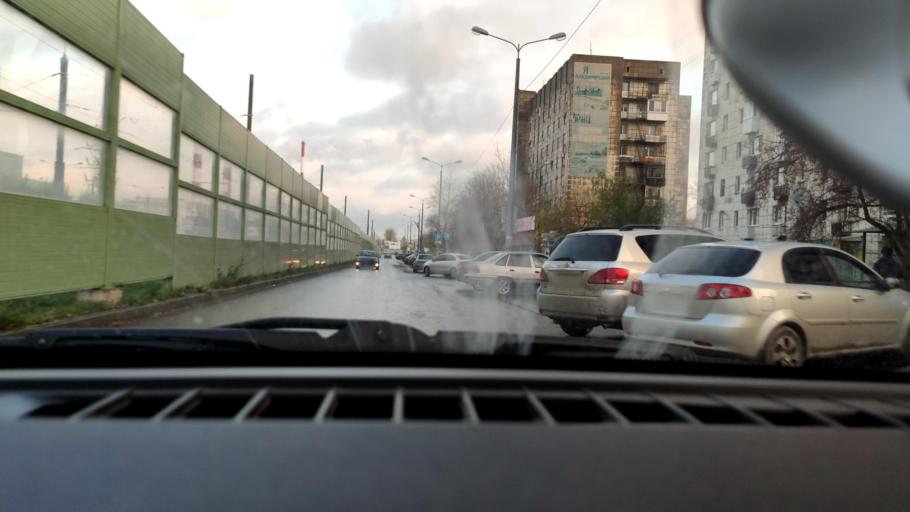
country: RU
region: Perm
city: Perm
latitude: 57.9708
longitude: 56.2616
